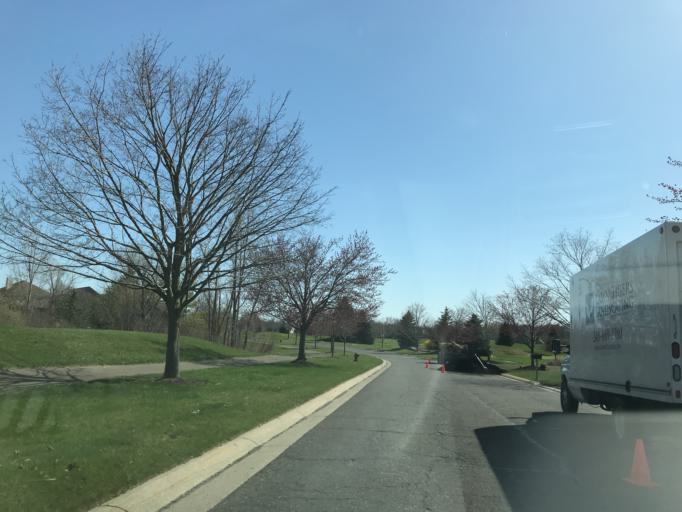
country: US
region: Michigan
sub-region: Oakland County
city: South Lyon
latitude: 42.4599
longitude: -83.5807
